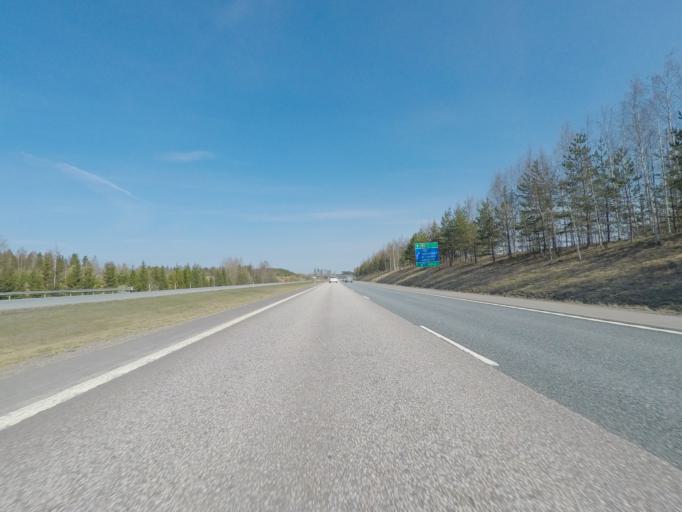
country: FI
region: Uusimaa
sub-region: Helsinki
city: Jaervenpaeae
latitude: 60.4926
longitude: 25.1359
